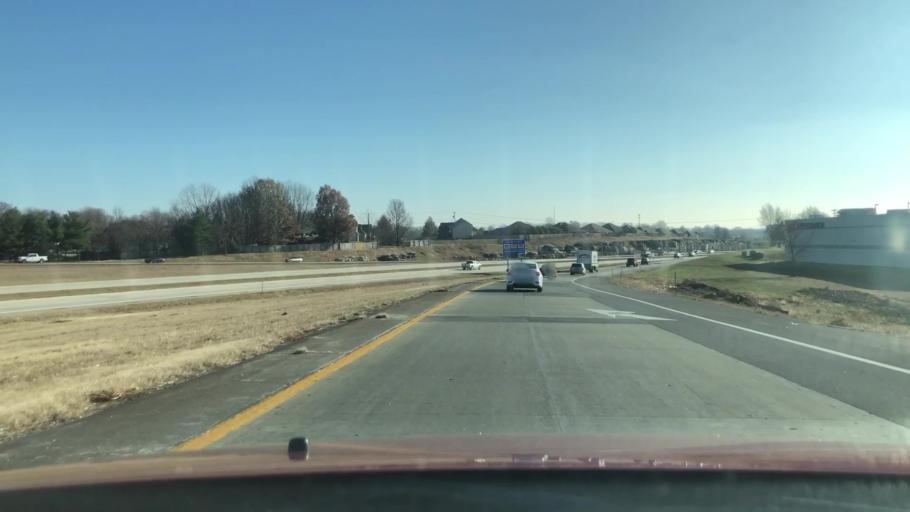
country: US
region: Missouri
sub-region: Greene County
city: Battlefield
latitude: 37.1415
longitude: -93.3179
